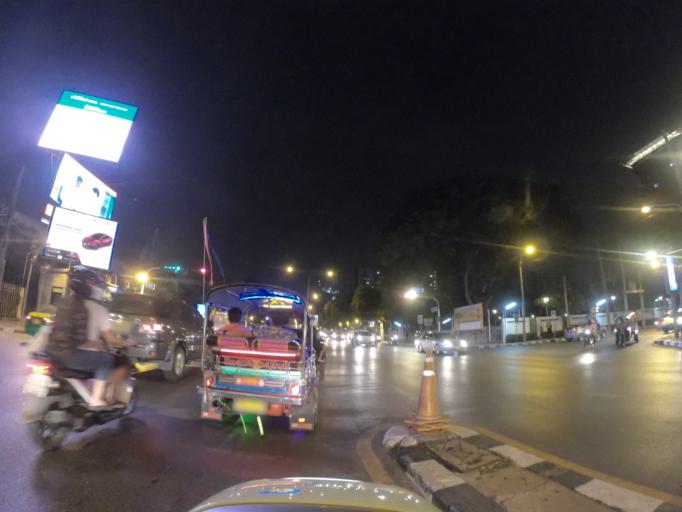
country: TH
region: Bangkok
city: Pathum Wan
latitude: 13.7428
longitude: 100.5303
